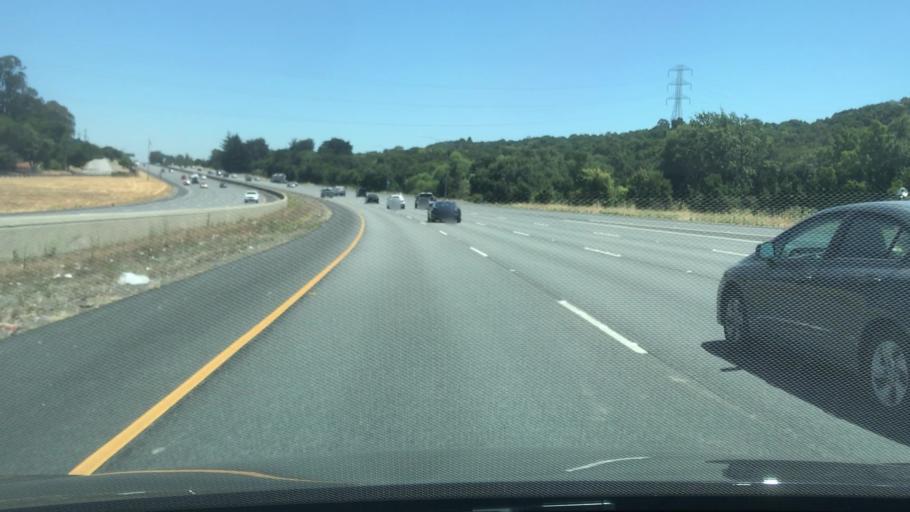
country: US
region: California
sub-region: San Mateo County
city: Emerald Lake Hills
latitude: 37.4580
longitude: -122.2889
